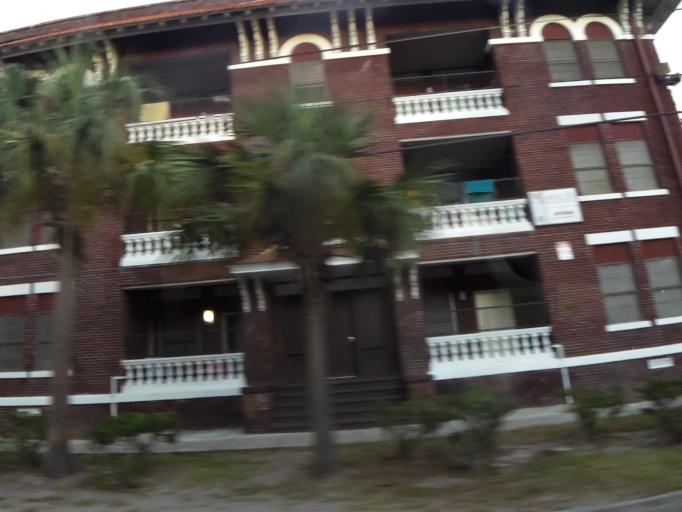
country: US
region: Florida
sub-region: Duval County
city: Jacksonville
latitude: 30.3377
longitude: -81.6517
